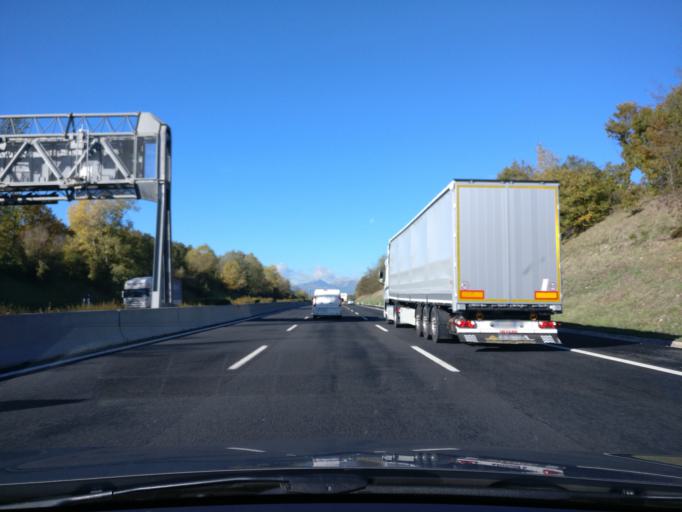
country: IT
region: Latium
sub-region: Provincia di Frosinone
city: Ceprano
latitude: 41.5469
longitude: 13.4758
